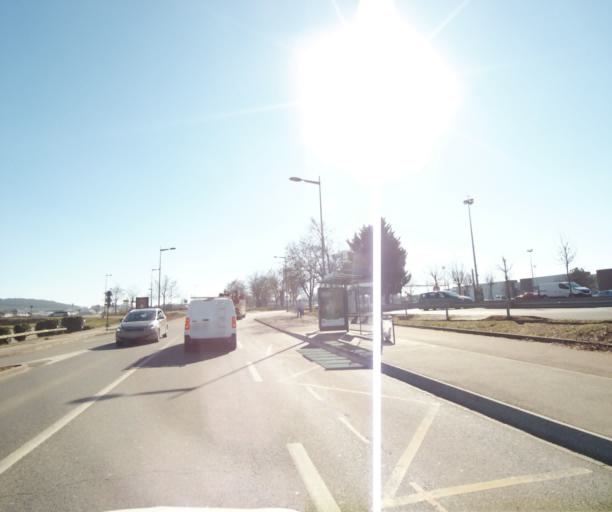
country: FR
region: Lorraine
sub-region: Departement de Meurthe-et-Moselle
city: Pulnoy
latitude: 48.7052
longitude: 6.2456
